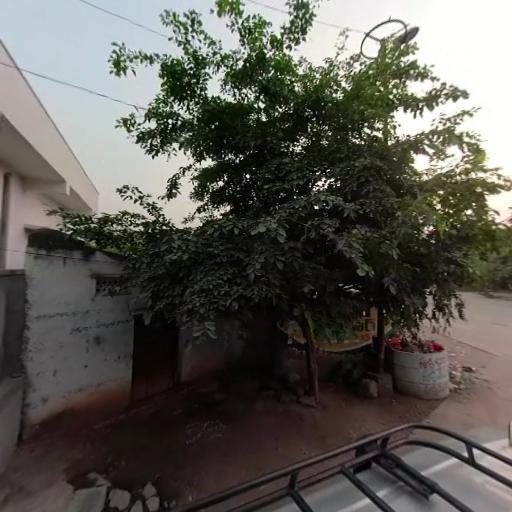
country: IN
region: Telangana
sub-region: Nalgonda
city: Suriapet
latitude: 17.1062
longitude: 79.5283
